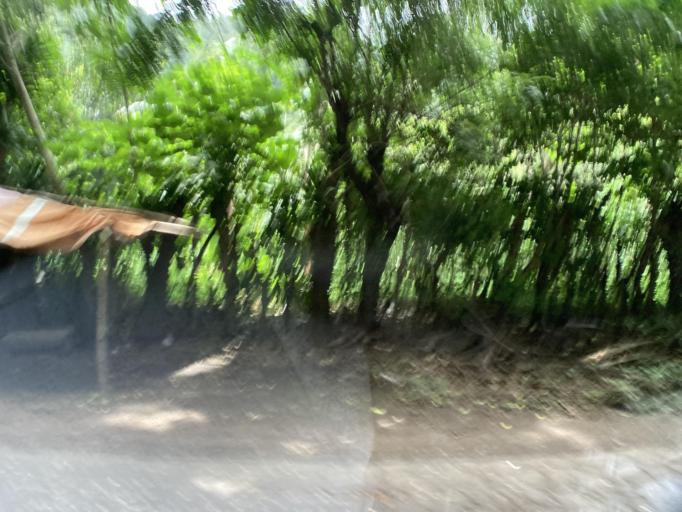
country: GT
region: Guatemala
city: Villa Canales
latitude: 14.4191
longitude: -90.5418
